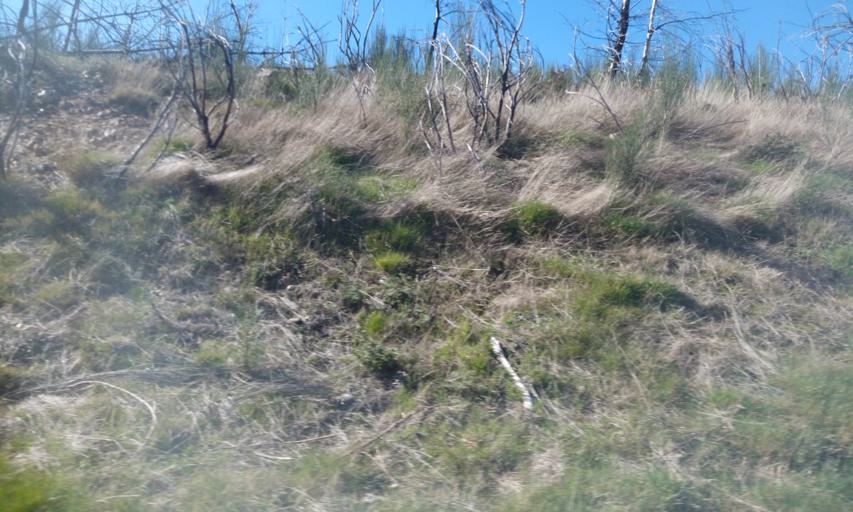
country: PT
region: Guarda
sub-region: Manteigas
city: Manteigas
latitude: 40.4938
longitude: -7.5422
